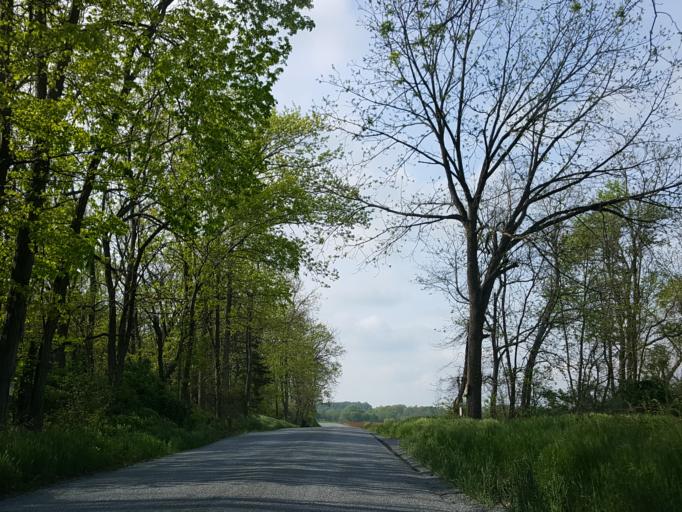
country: US
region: Pennsylvania
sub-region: Lebanon County
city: Campbelltown
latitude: 40.2207
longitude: -76.5739
